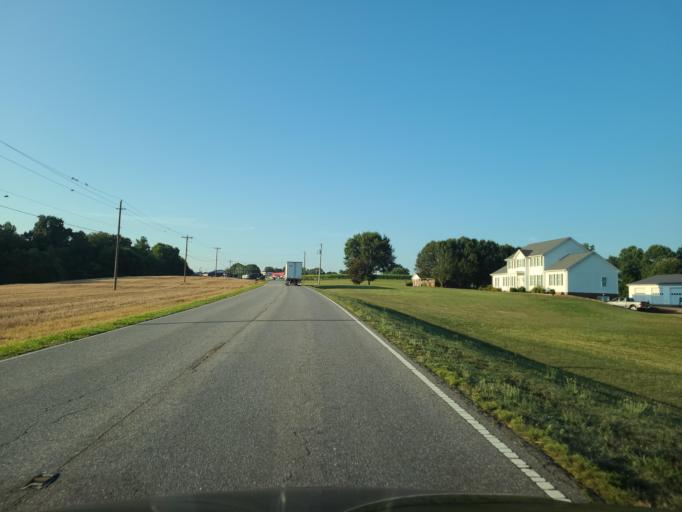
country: US
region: North Carolina
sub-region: Catawba County
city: Mountain View
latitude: 35.6358
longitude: -81.3816
